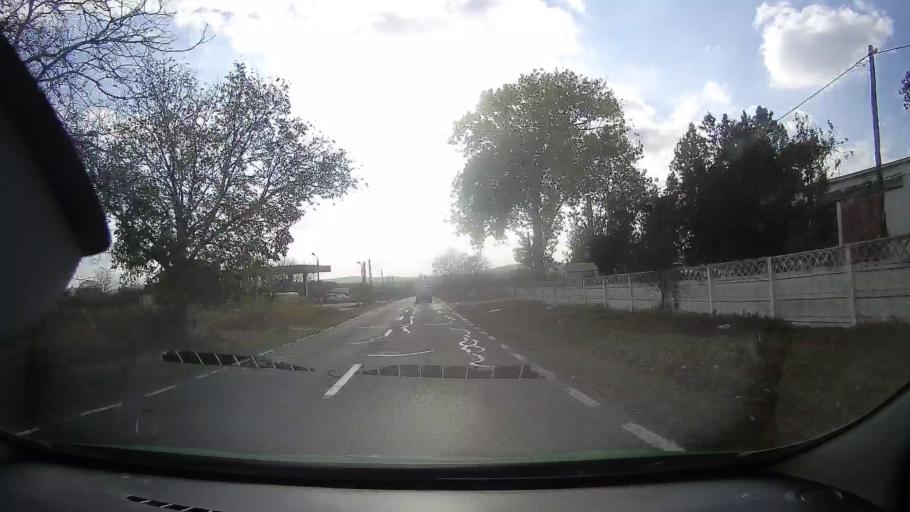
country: RO
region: Tulcea
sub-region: Comuna Nalbant
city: Nalbant
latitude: 45.0530
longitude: 28.6180
